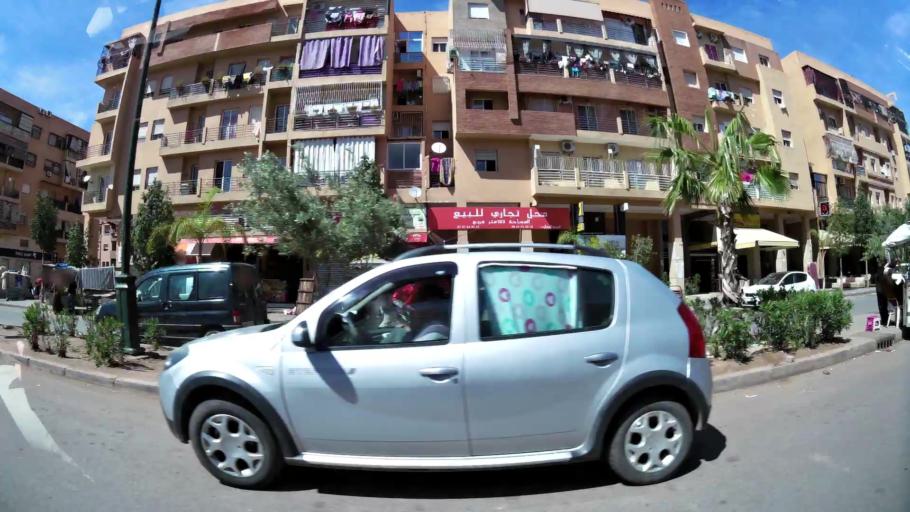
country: MA
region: Marrakech-Tensift-Al Haouz
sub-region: Marrakech
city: Marrakesh
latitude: 31.6396
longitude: -8.0770
